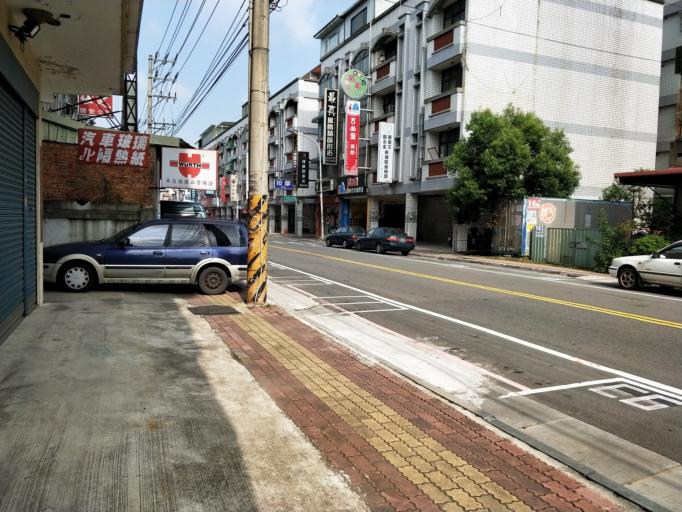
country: TW
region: Taiwan
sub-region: Hsinchu
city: Zhubei
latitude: 24.8266
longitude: 121.0841
